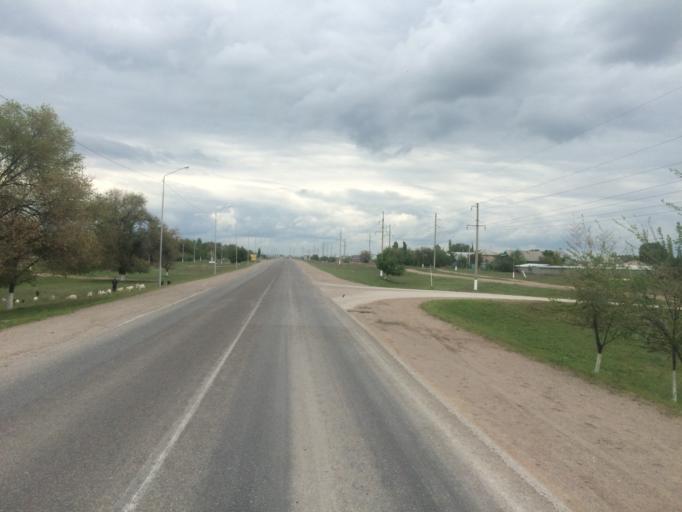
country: KG
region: Chuy
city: Sokuluk
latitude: 43.2500
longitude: 74.2893
